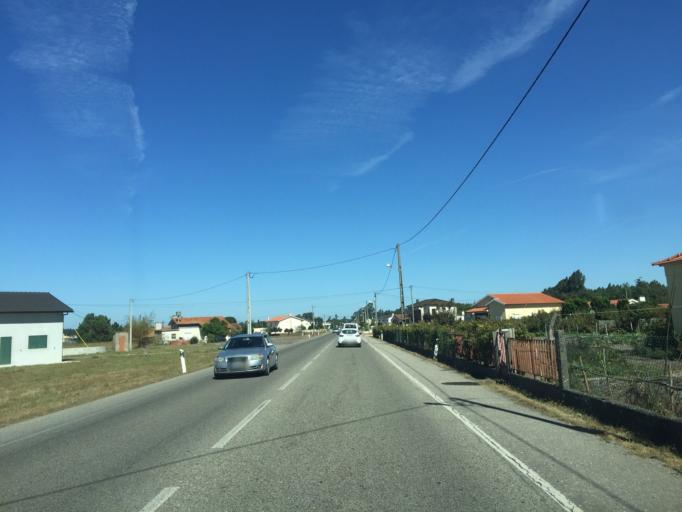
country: PT
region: Coimbra
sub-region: Figueira da Foz
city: Alhadas
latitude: 40.2394
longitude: -8.7933
